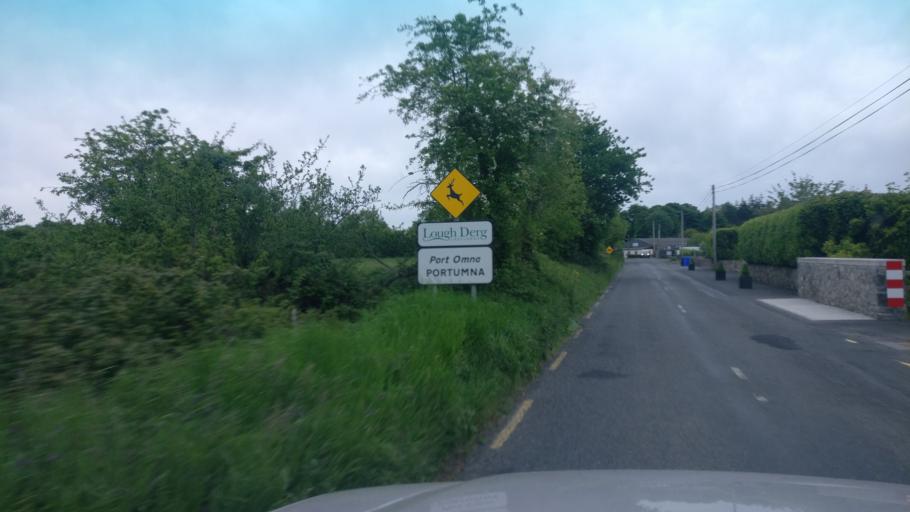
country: IE
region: Connaught
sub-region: County Galway
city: Portumna
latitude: 53.0919
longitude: -8.2344
